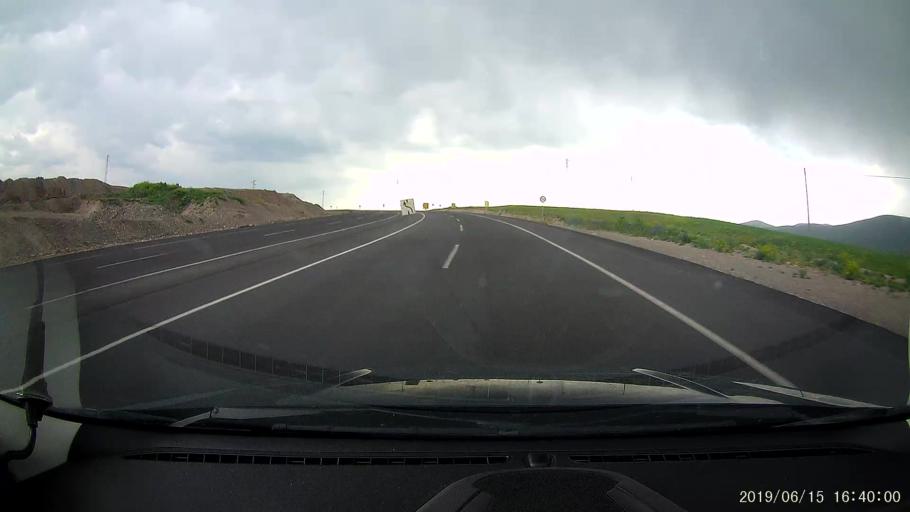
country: TR
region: Ardahan
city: Haskoy
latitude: 40.9749
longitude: 42.8934
